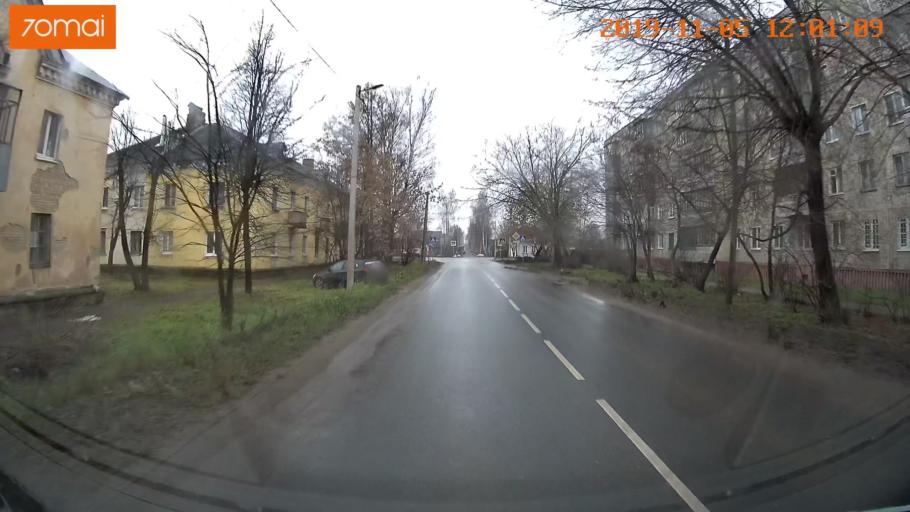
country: RU
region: Ivanovo
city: Kokhma
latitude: 56.9739
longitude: 41.0459
